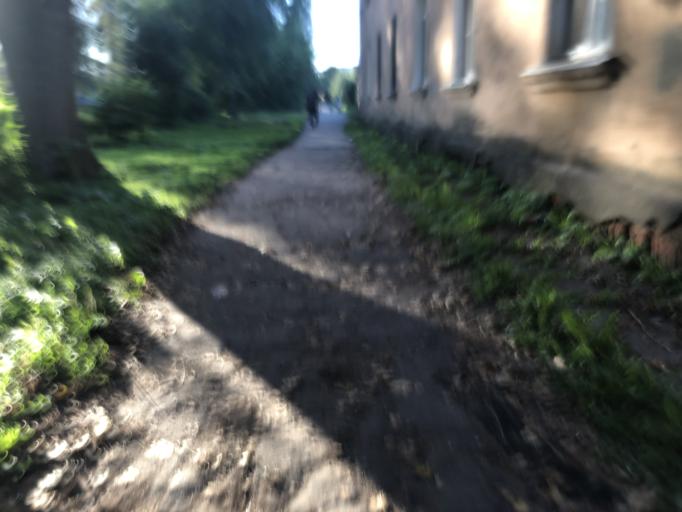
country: RU
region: Tverskaya
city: Rzhev
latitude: 56.2416
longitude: 34.3179
